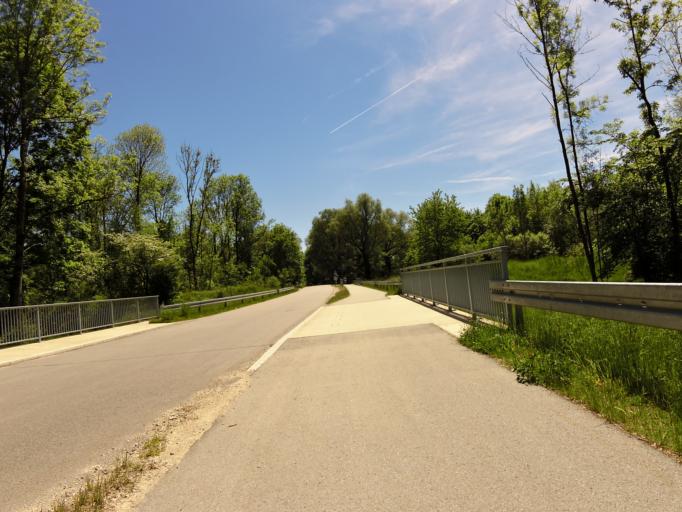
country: DE
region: Bavaria
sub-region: Upper Bavaria
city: Marzling
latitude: 48.4043
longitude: 11.7918
